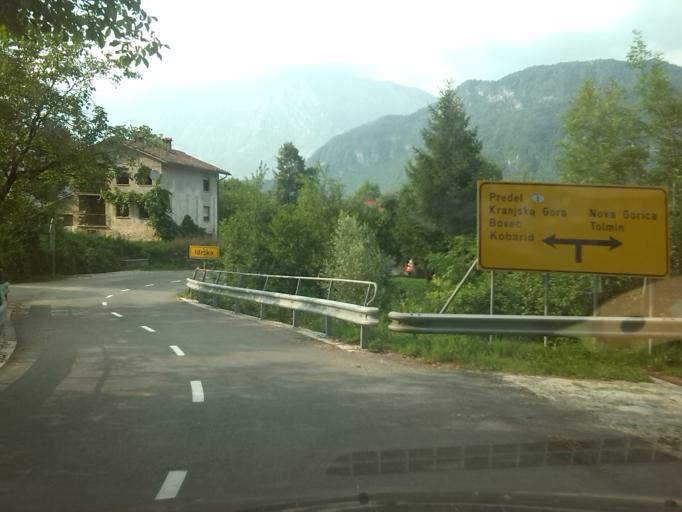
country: SI
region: Kobarid
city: Kobarid
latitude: 46.2302
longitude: 13.5914
